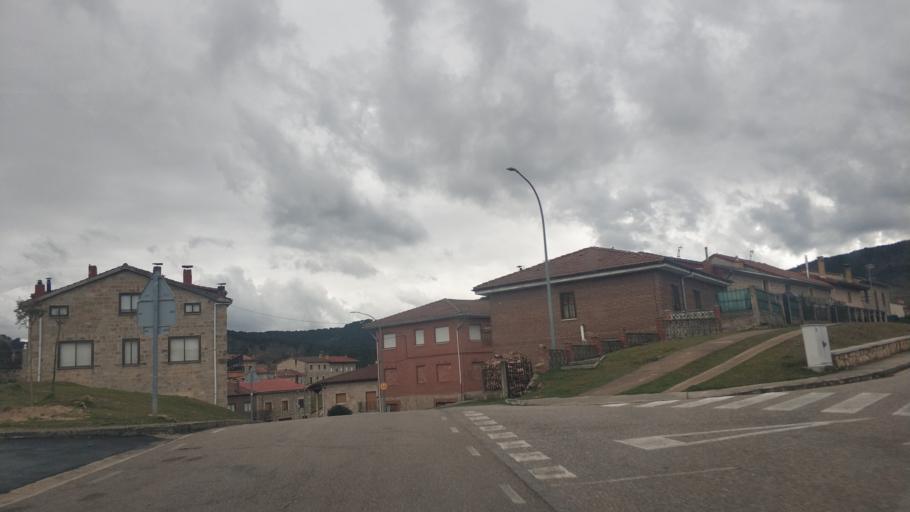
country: ES
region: Castille and Leon
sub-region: Provincia de Burgos
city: Canicosa de la Sierra
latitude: 41.9385
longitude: -3.0387
